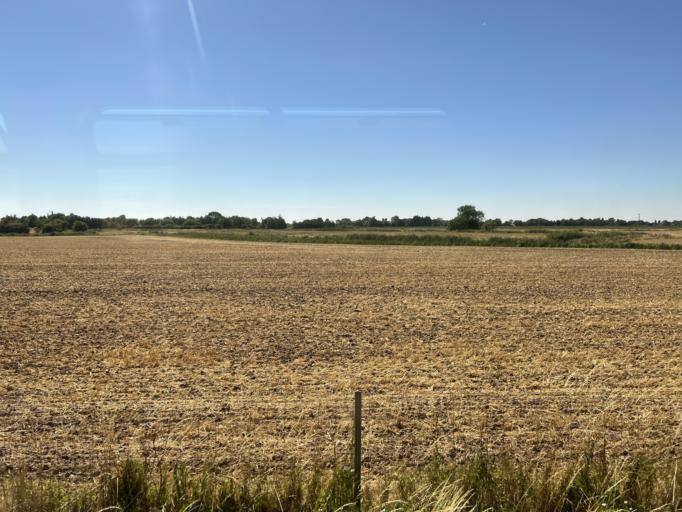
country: GB
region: England
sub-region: Lincolnshire
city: Wainfleet All Saints
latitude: 53.1144
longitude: 0.2146
